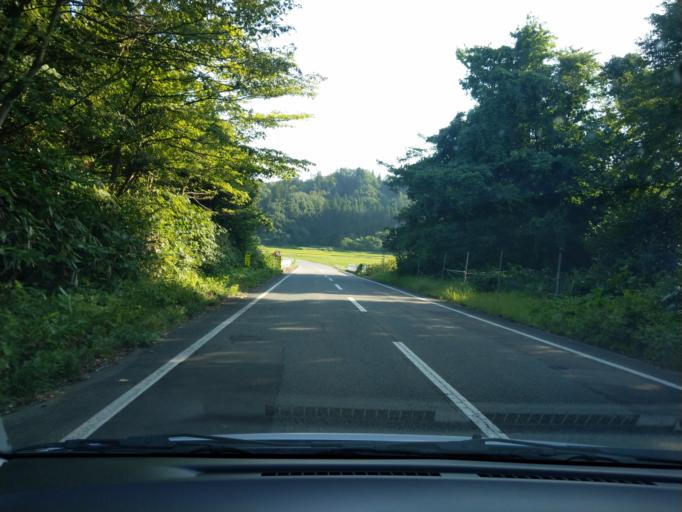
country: JP
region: Akita
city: Akita
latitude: 39.5948
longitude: 140.2333
